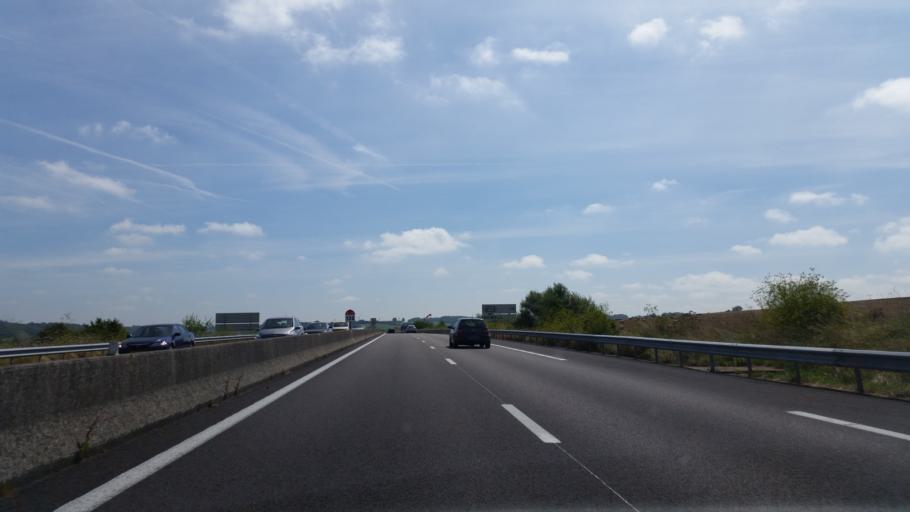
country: FR
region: Haute-Normandie
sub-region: Departement de la Seine-Maritime
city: Serqueux
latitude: 49.7375
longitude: 1.5462
